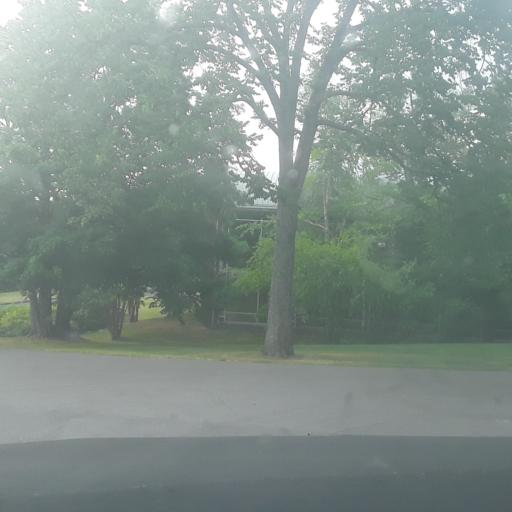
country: US
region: Tennessee
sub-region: Davidson County
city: Oak Hill
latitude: 36.0645
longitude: -86.7474
